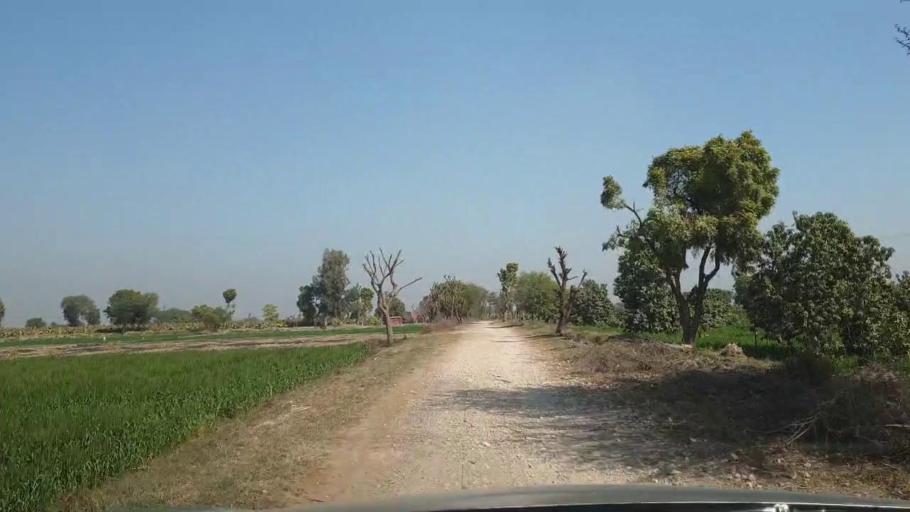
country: PK
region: Sindh
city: Tando Allahyar
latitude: 25.5903
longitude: 68.6504
